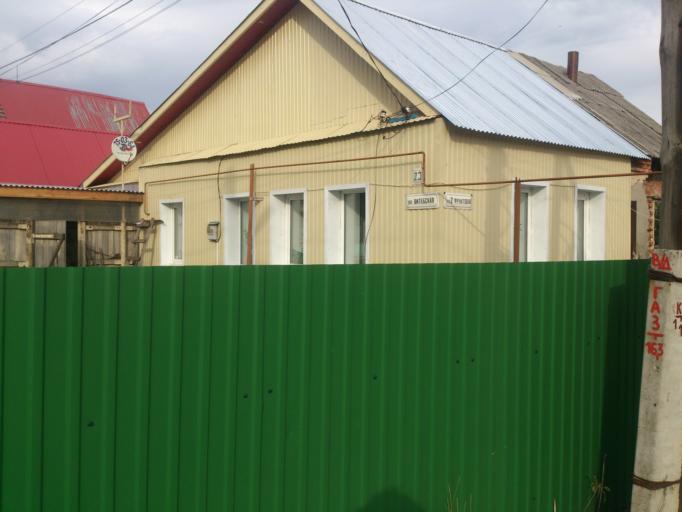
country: RU
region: Ulyanovsk
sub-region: Ulyanovskiy Rayon
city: Ulyanovsk
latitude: 54.2809
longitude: 48.3055
